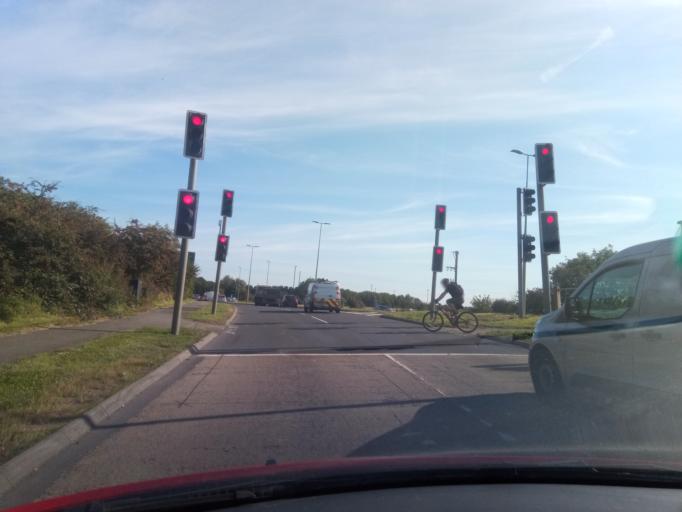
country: GB
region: England
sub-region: Sunderland
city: Washington
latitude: 54.9071
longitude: -1.5592
